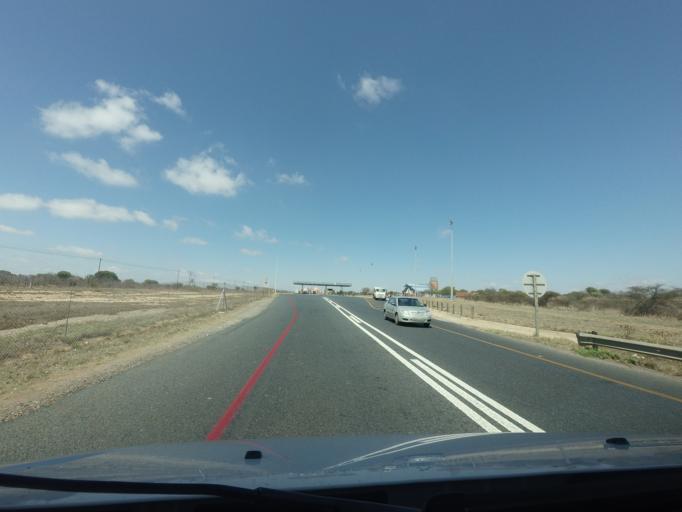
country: ZA
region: Limpopo
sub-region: Vhembe District Municipality
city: Louis Trichardt
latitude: -23.3656
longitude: 29.7761
